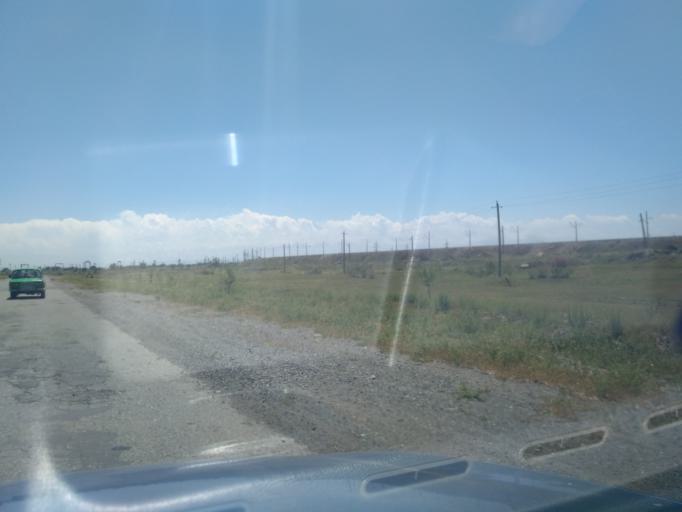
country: TJ
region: Viloyati Sughd
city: Zafarobod
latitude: 40.2167
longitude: 68.8556
